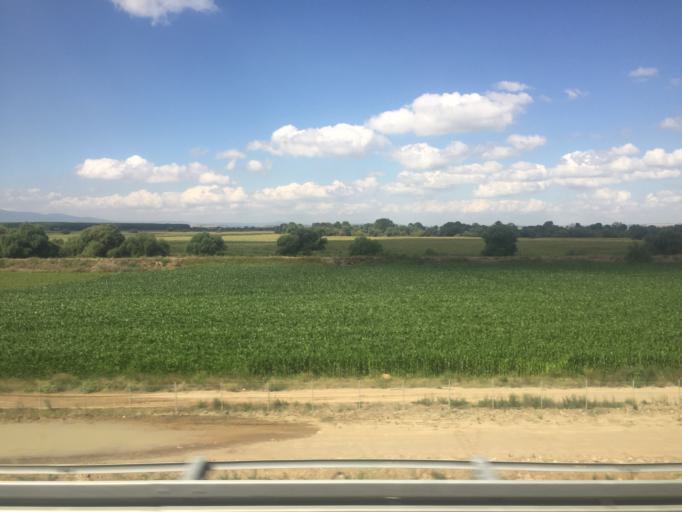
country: TR
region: Bursa
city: Tatkavakli
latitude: 40.1061
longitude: 28.2775
